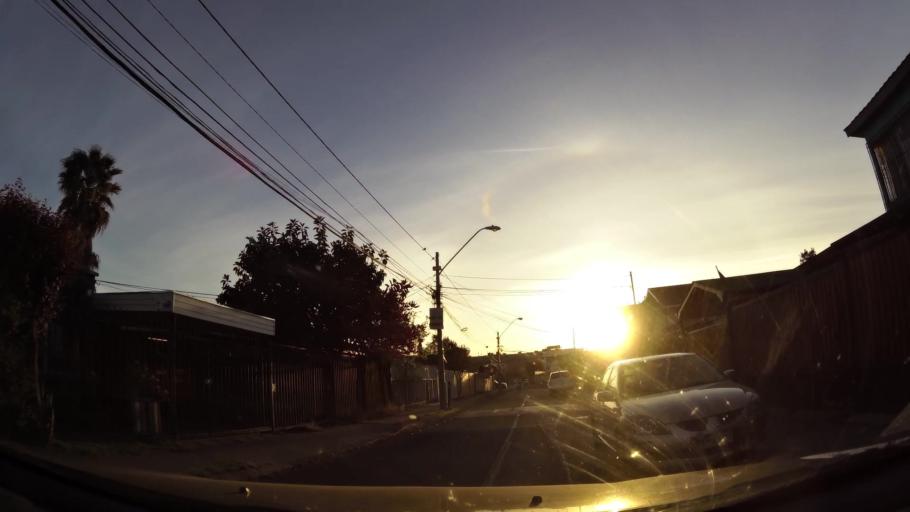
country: CL
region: Santiago Metropolitan
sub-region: Provincia de Cordillera
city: Puente Alto
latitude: -33.5997
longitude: -70.5713
